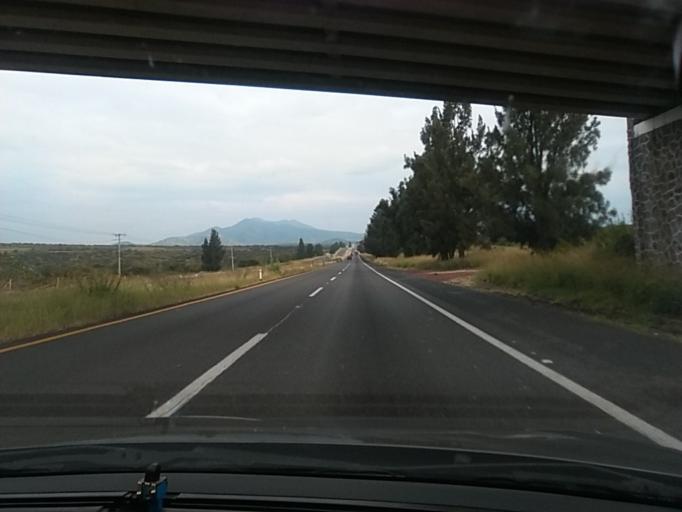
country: MX
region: Michoacan
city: Churintzio
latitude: 20.1641
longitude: -102.1253
